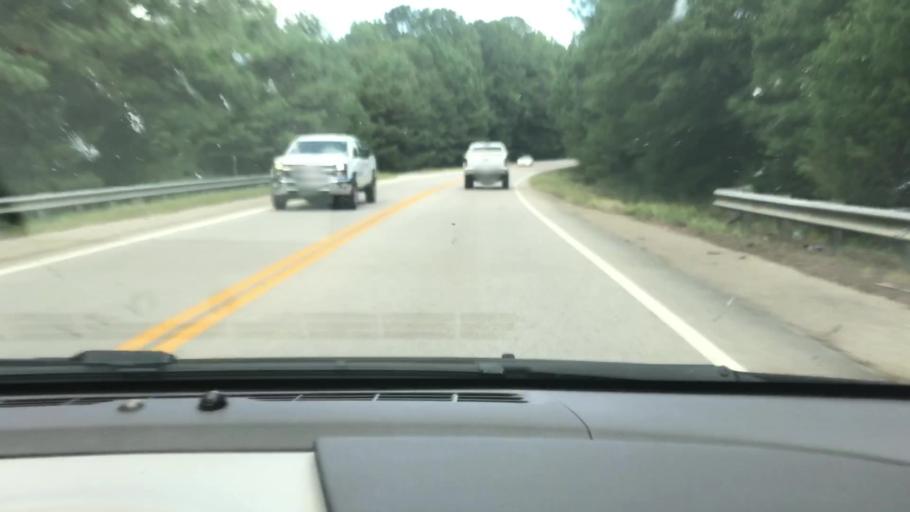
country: US
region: Georgia
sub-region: Troup County
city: La Grange
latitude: 32.9729
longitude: -85.0259
